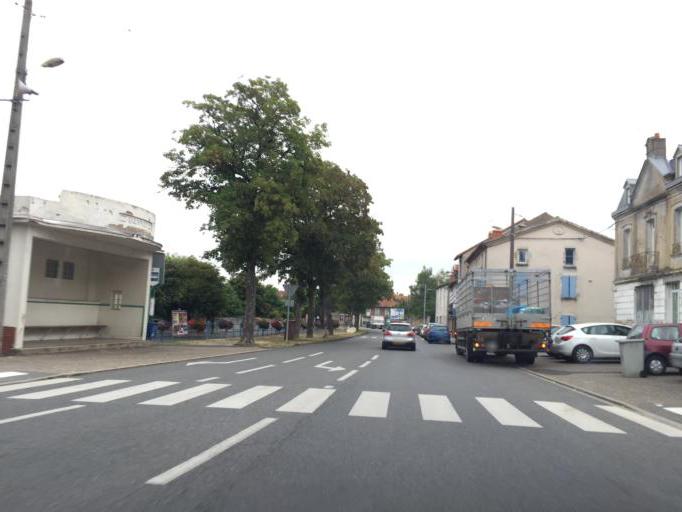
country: FR
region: Auvergne
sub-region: Departement de l'Allier
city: Gannat
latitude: 46.0979
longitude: 3.1985
